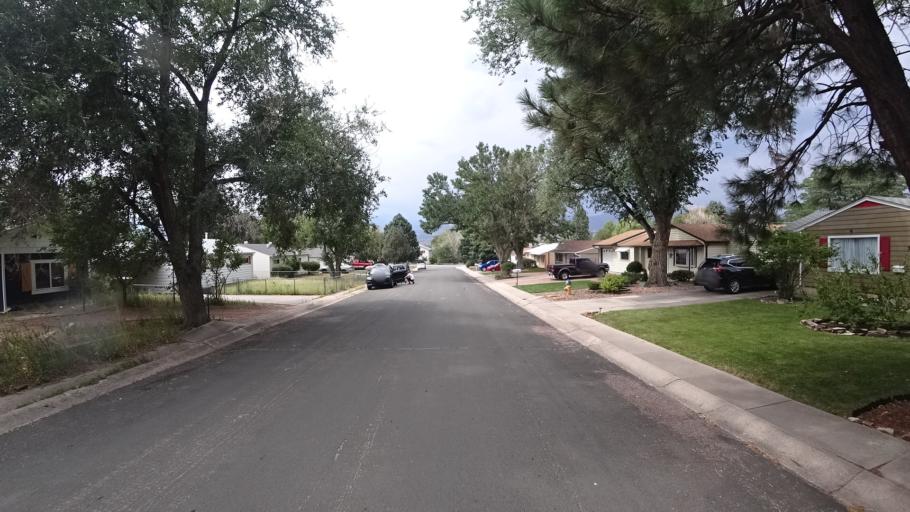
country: US
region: Colorado
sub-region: El Paso County
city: Colorado Springs
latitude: 38.8928
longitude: -104.8134
